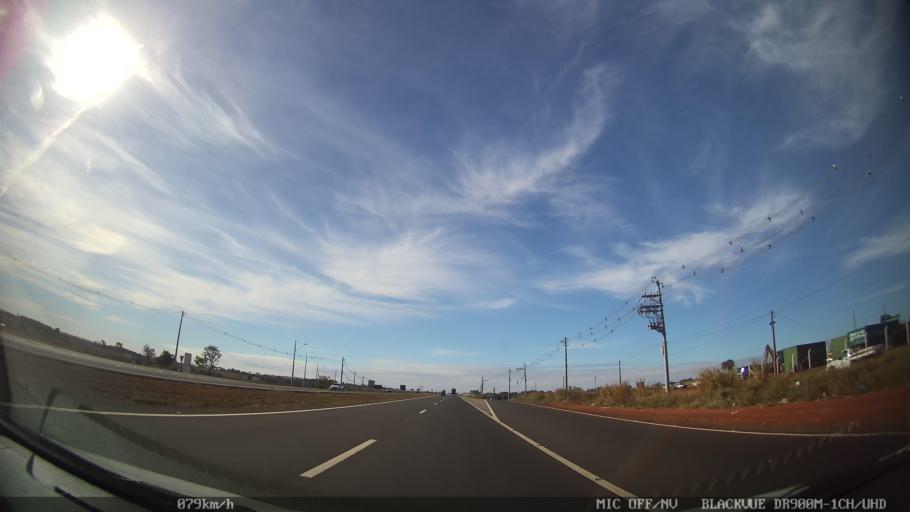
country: BR
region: Sao Paulo
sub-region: Sao Jose Do Rio Preto
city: Sao Jose do Rio Preto
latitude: -20.7647
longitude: -49.3474
